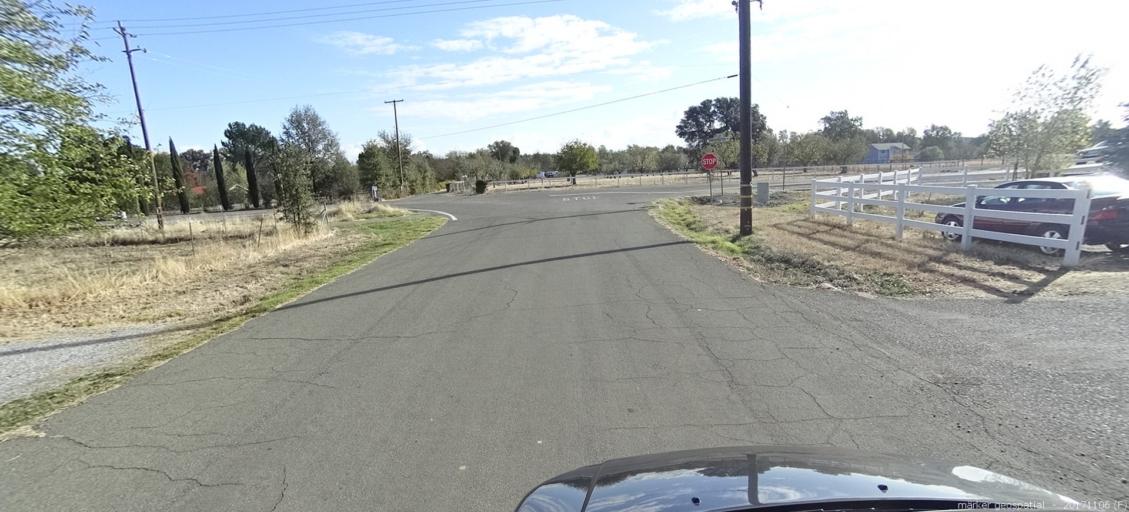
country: US
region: California
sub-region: Shasta County
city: Palo Cedro
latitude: 40.5433
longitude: -122.2393
